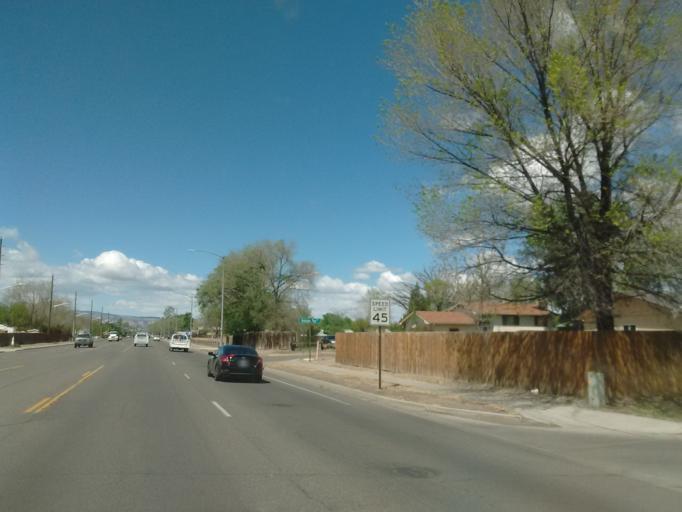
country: US
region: Colorado
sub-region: Mesa County
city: Fruitvale
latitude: 39.0919
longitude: -108.4979
